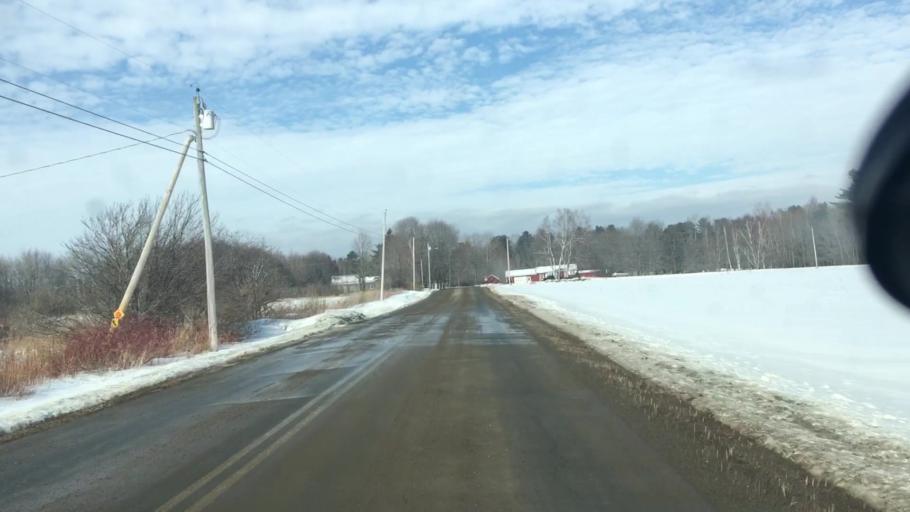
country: US
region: Maine
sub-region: Penobscot County
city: Levant
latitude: 44.8604
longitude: -68.8792
